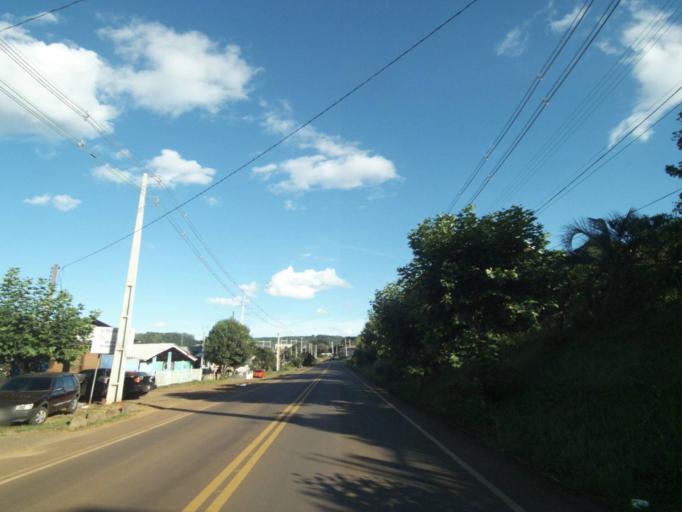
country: BR
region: Parana
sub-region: Uniao Da Vitoria
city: Uniao da Vitoria
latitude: -26.1673
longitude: -51.5335
